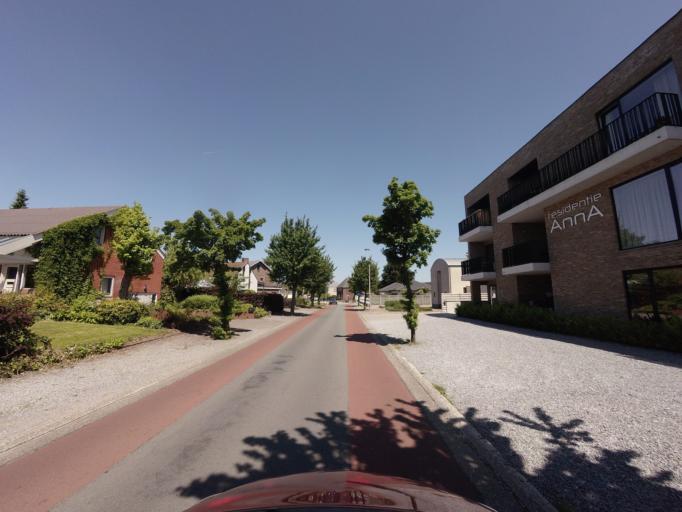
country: BE
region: Flanders
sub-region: Provincie Limburg
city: Lommel
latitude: 51.2357
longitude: 5.3153
